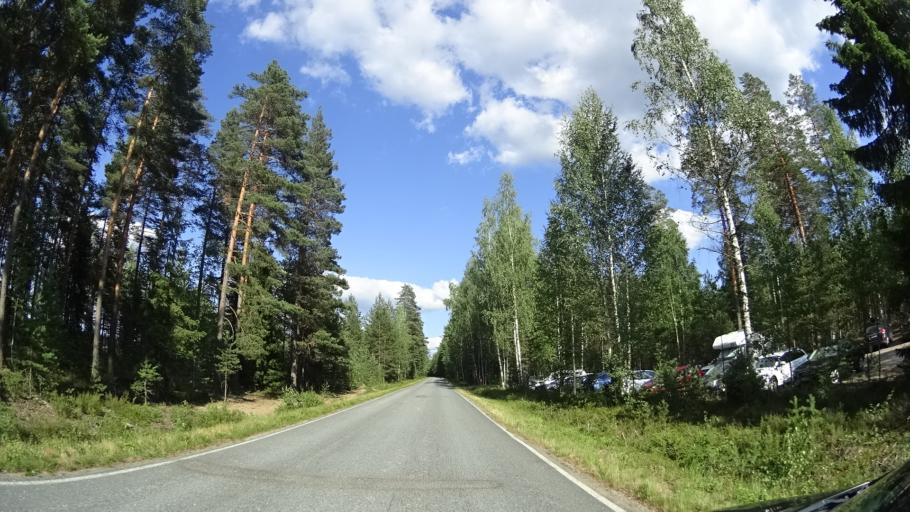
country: FI
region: Uusimaa
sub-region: Helsinki
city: Kaerkoelae
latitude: 60.7394
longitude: 24.0976
